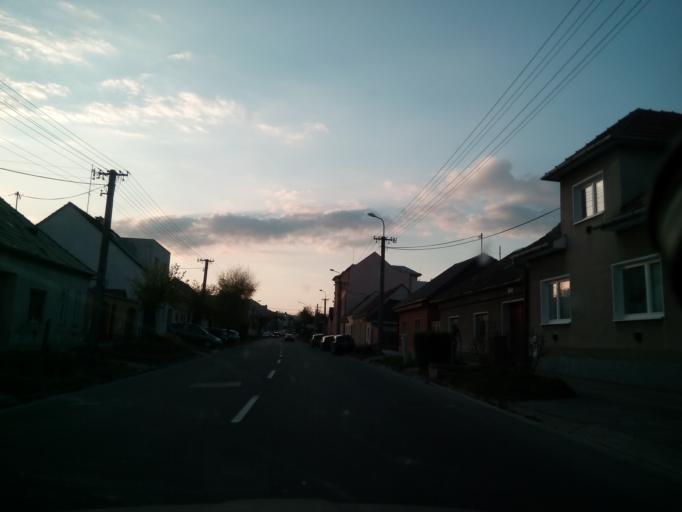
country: SK
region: Trnavsky
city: Vrbove
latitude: 48.6183
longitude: 17.7288
